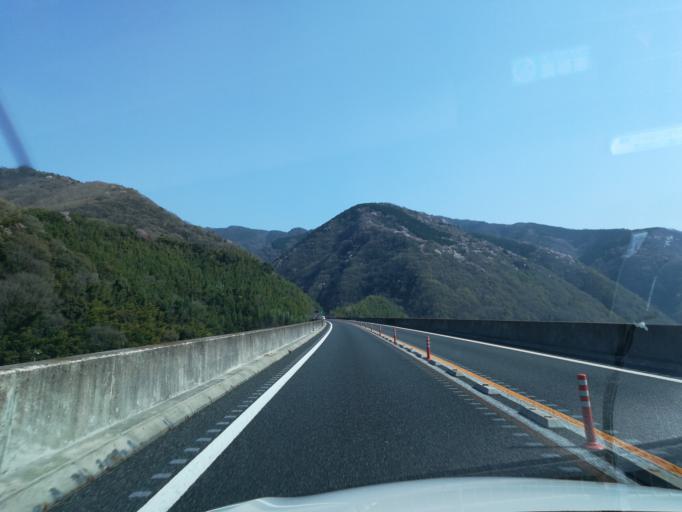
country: JP
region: Tokushima
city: Ikedacho
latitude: 34.0455
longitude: 133.9126
